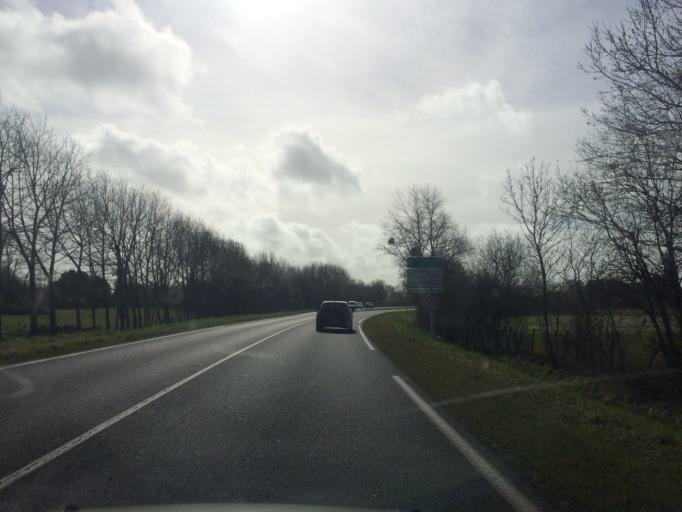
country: FR
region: Pays de la Loire
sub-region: Departement de la Loire-Atlantique
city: Besne
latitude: 47.3838
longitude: -2.0952
